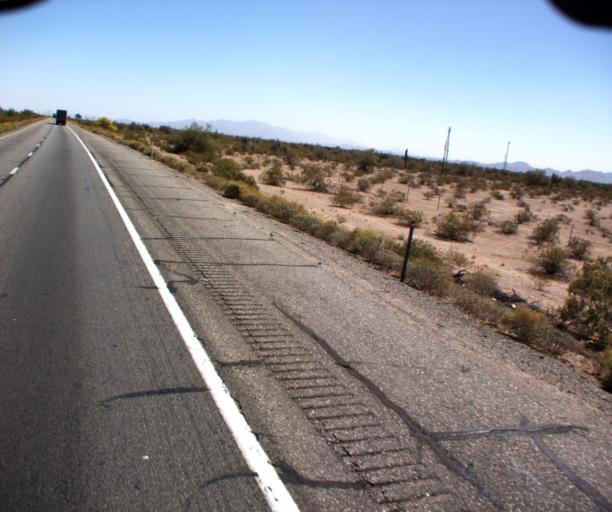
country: US
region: Arizona
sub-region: Maricopa County
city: Buckeye
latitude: 33.4310
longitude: -112.6444
